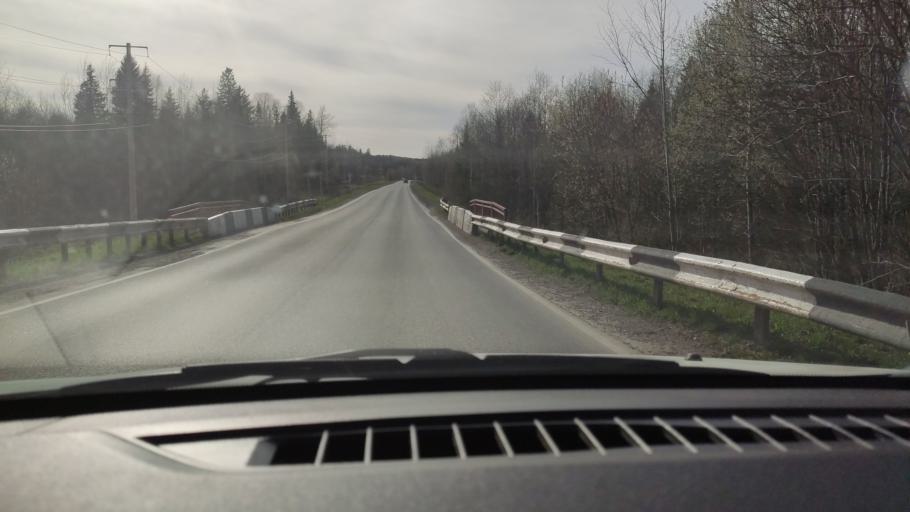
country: RU
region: Perm
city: Novyye Lyady
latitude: 57.9579
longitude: 56.5574
